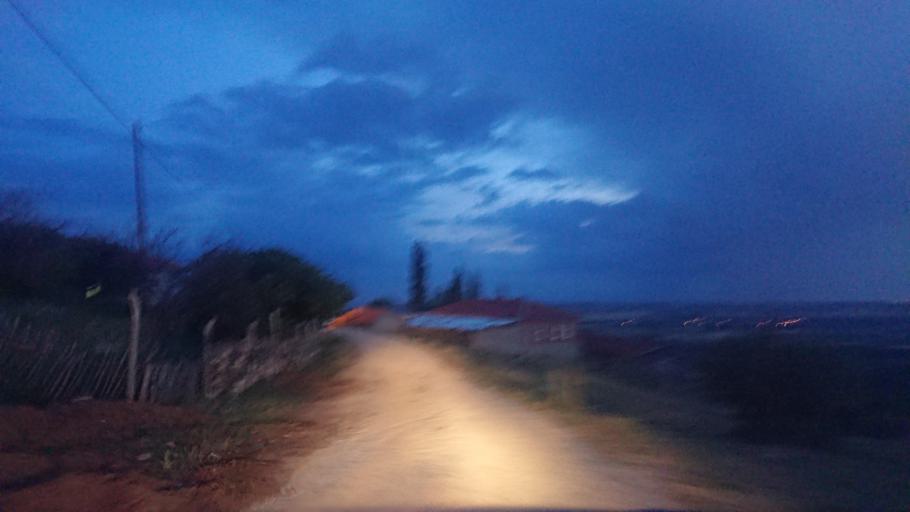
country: TR
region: Aksaray
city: Ortakoy
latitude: 38.6333
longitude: 34.0144
